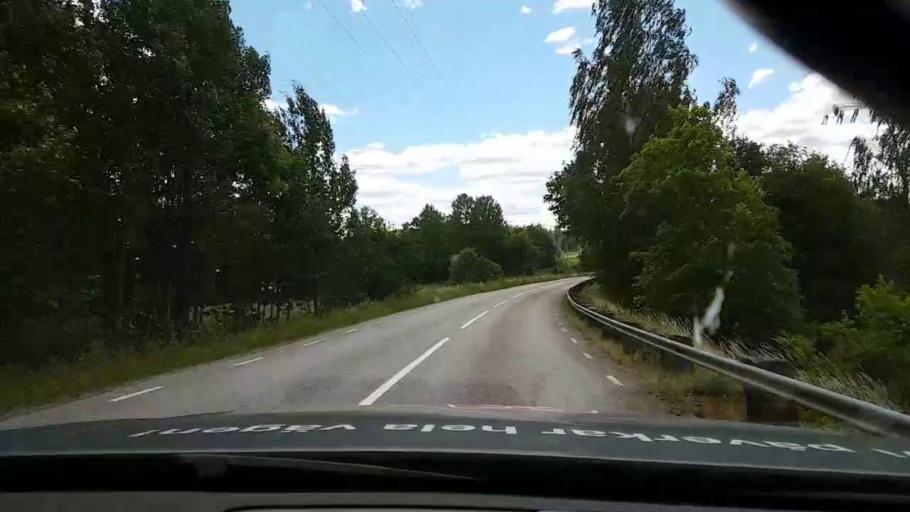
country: SE
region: Kalmar
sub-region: Vasterviks Kommun
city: Overum
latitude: 58.0573
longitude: 16.4064
